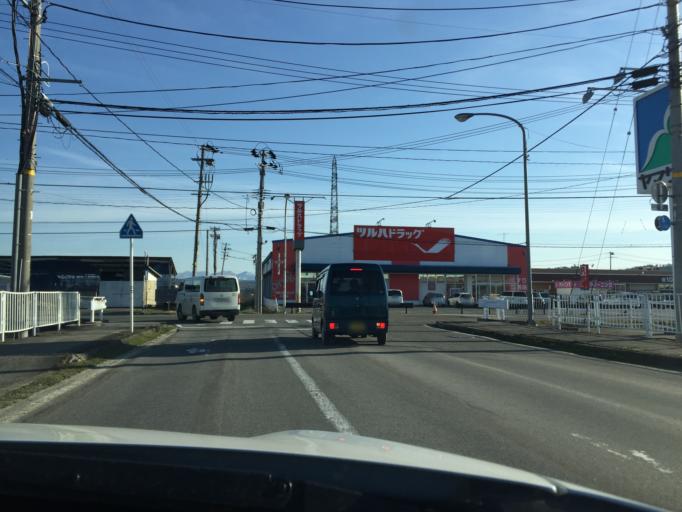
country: JP
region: Yamagata
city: Nagai
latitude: 38.0017
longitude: 140.0519
